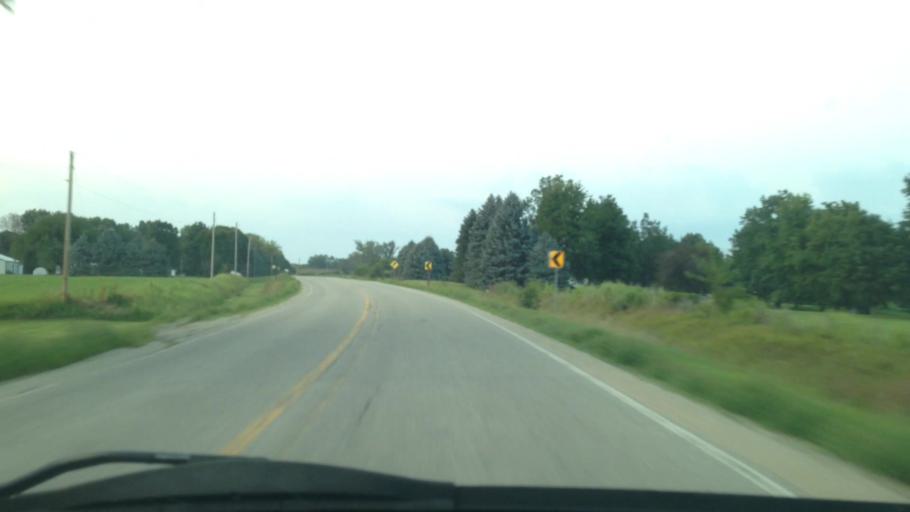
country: US
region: Iowa
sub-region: Benton County
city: Urbana
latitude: 42.1533
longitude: -91.8779
